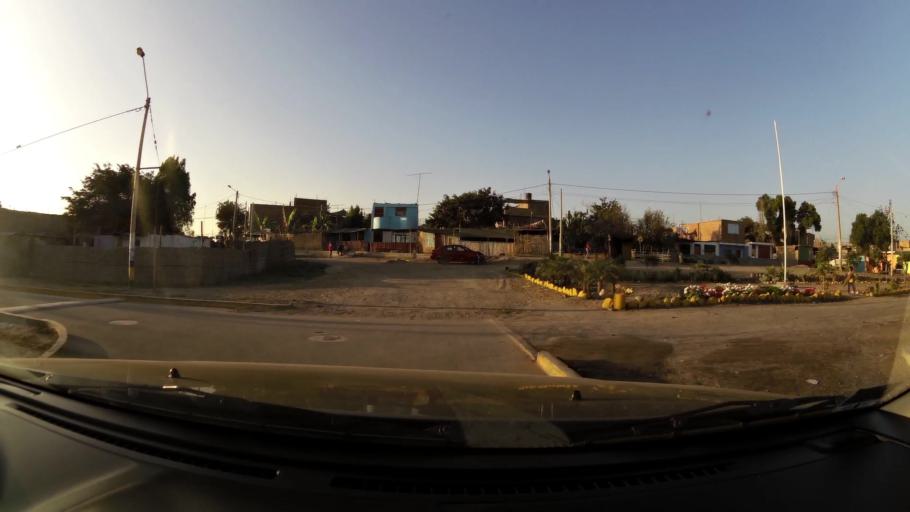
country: PE
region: Ica
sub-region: Provincia de Pisco
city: Villa Tupac Amaru
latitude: -13.7068
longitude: -76.1504
